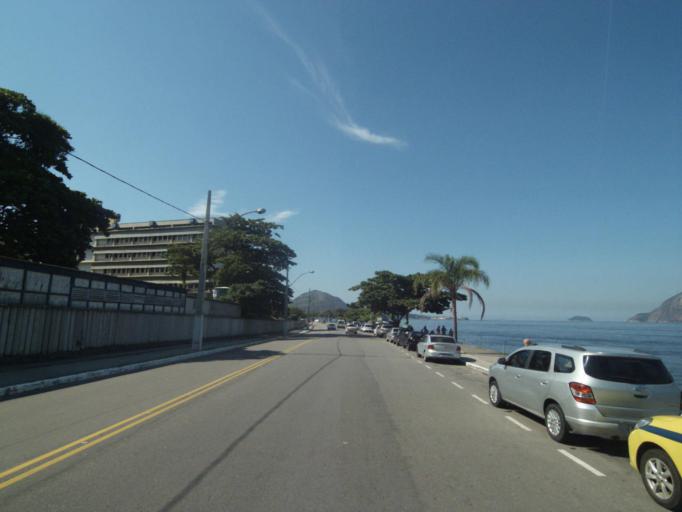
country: BR
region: Rio de Janeiro
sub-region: Niteroi
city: Niteroi
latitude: -22.9038
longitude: -43.1355
